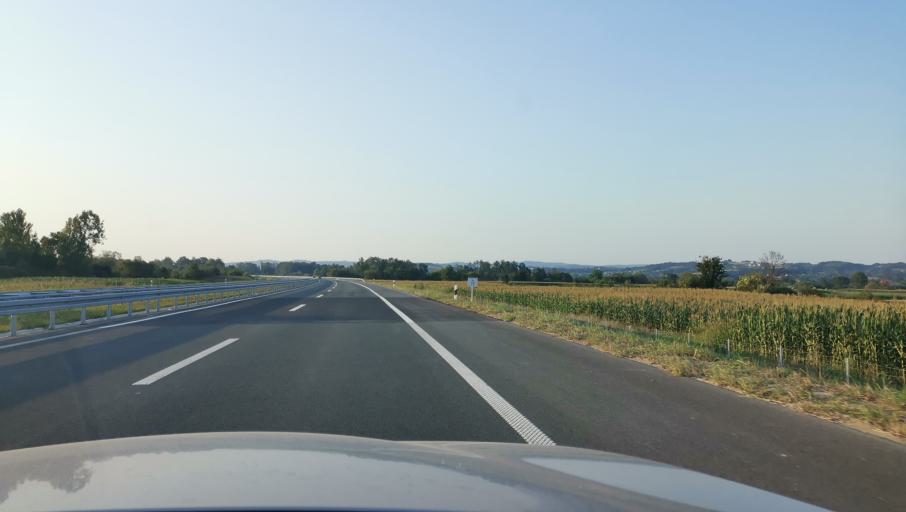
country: RS
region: Central Serbia
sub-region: Kolubarski Okrug
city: Ljig
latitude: 44.2599
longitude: 20.2712
